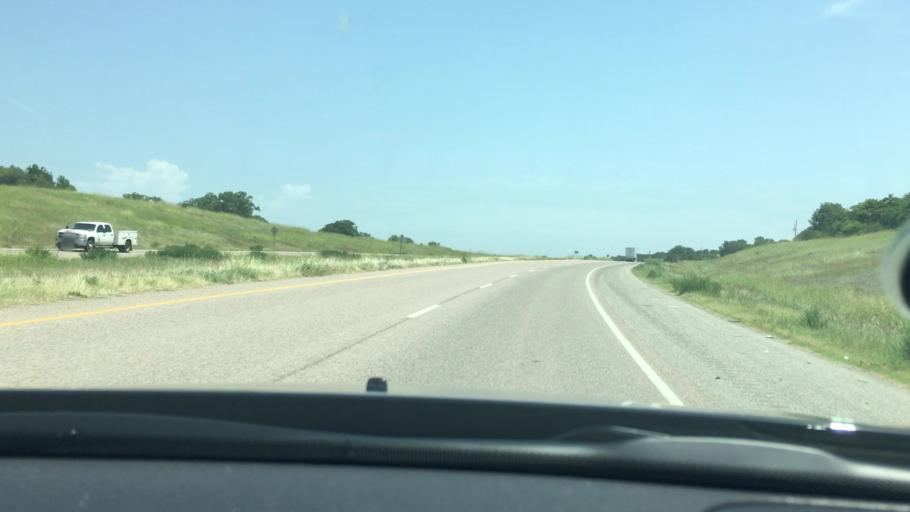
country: US
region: Oklahoma
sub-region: Pontotoc County
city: Ada
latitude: 34.8128
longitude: -96.6956
